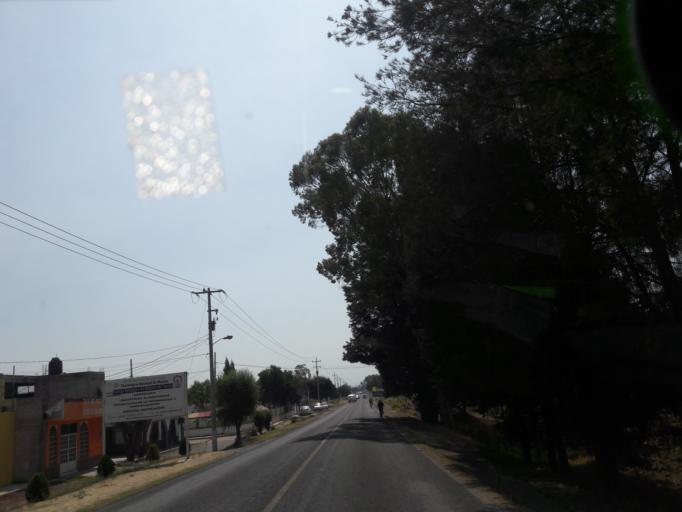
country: MX
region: Tlaxcala
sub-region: Ixtacuixtla de Mariano Matamoros
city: Villa Mariano Matamoros
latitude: 19.3102
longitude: -98.3832
